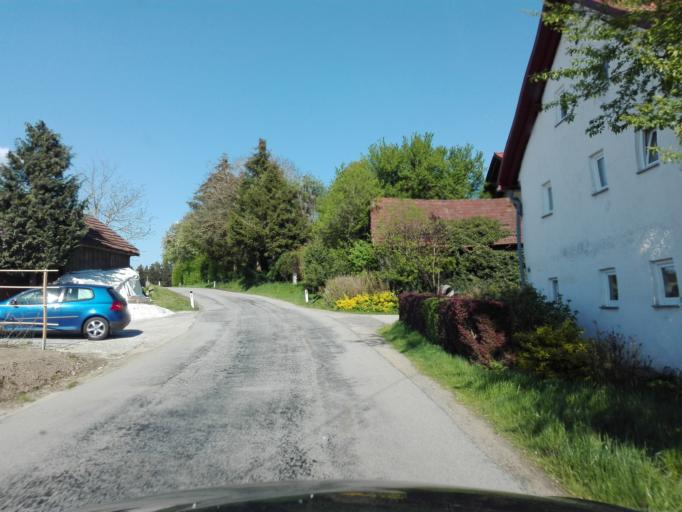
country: DE
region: Bavaria
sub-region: Lower Bavaria
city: Obernzell
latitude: 48.4993
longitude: 13.5851
